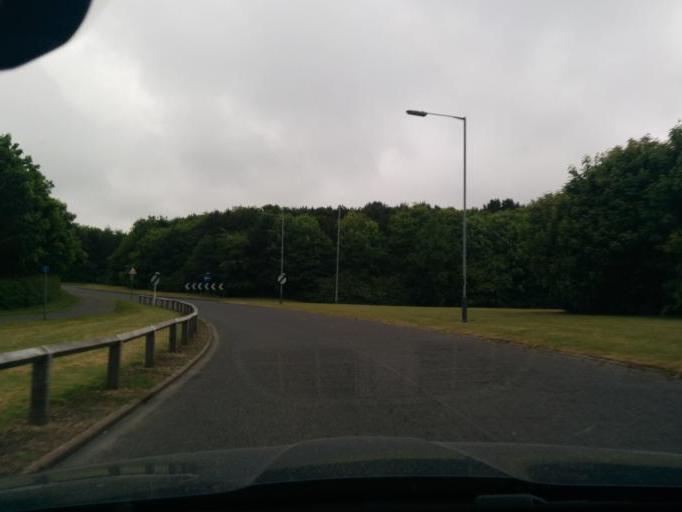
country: GB
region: England
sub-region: Northumberland
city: Cramlington
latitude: 55.0956
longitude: -1.5935
